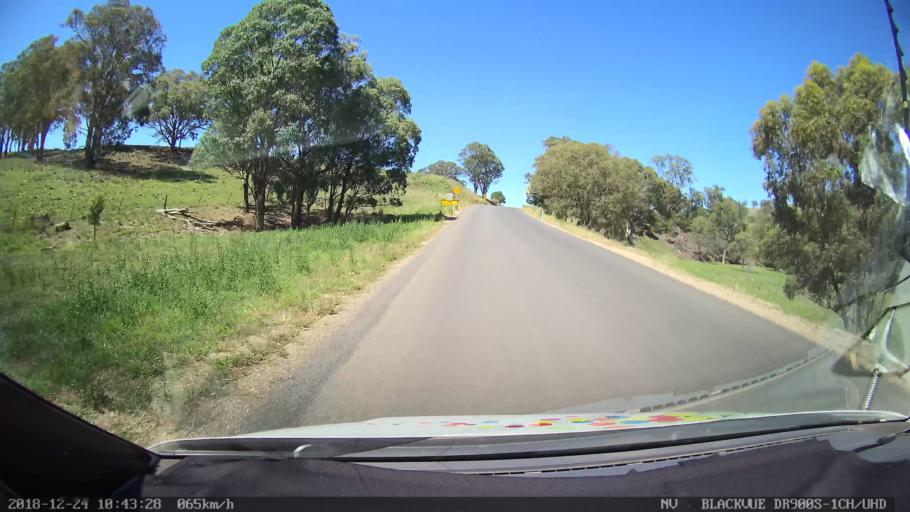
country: AU
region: New South Wales
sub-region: Upper Hunter Shire
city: Merriwa
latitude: -31.8830
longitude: 150.4462
